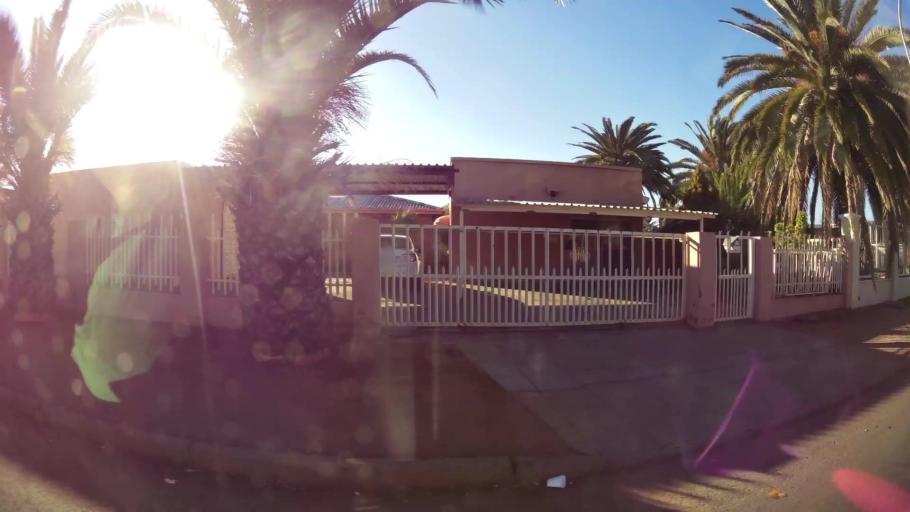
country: ZA
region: Northern Cape
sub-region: Frances Baard District Municipality
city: Kimberley
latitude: -28.7376
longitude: 24.7306
